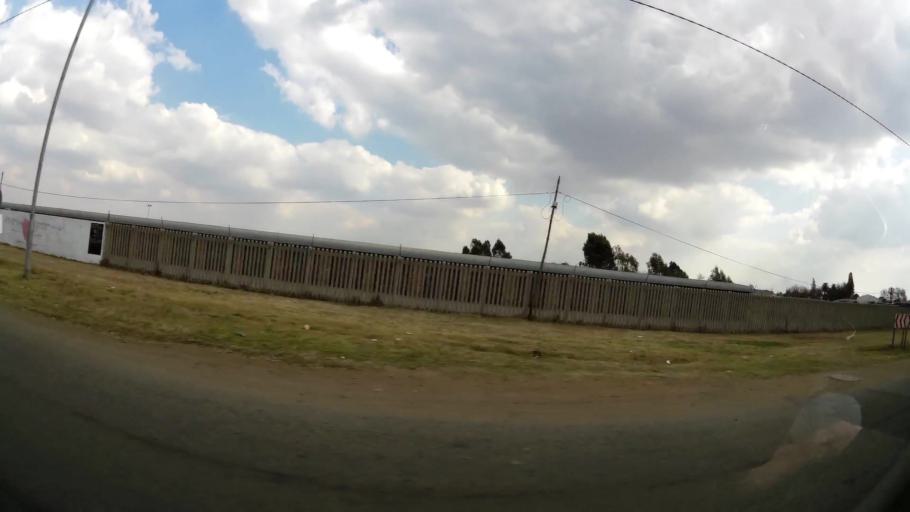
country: ZA
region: Gauteng
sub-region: Ekurhuleni Metropolitan Municipality
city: Benoni
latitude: -26.1100
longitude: 28.3702
